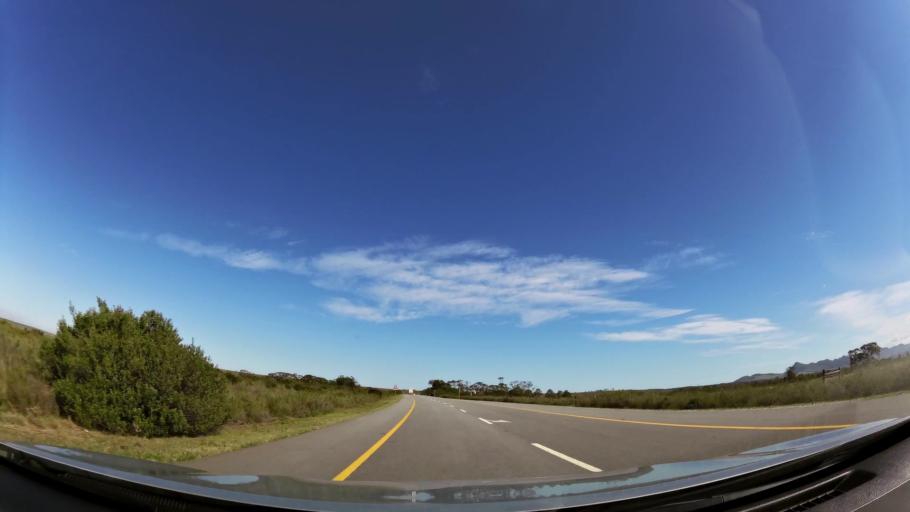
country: ZA
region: Eastern Cape
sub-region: Cacadu District Municipality
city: Kruisfontein
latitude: -34.0329
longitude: 24.5944
